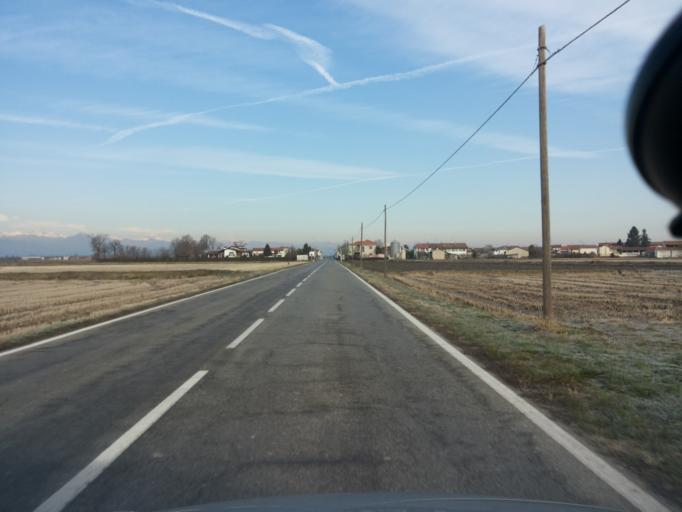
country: IT
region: Piedmont
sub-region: Provincia di Vercelli
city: Oldenico
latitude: 45.3981
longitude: 8.3792
